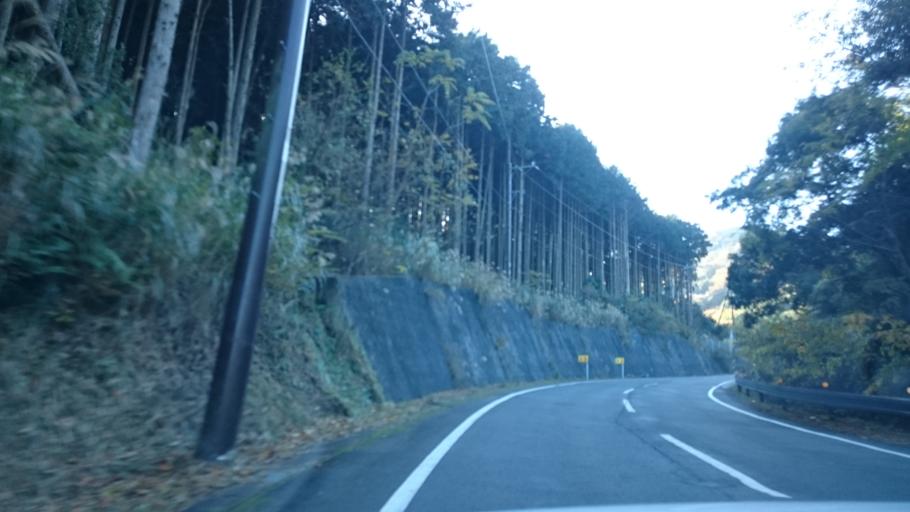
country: JP
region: Shizuoka
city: Heda
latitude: 35.0000
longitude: 138.8194
